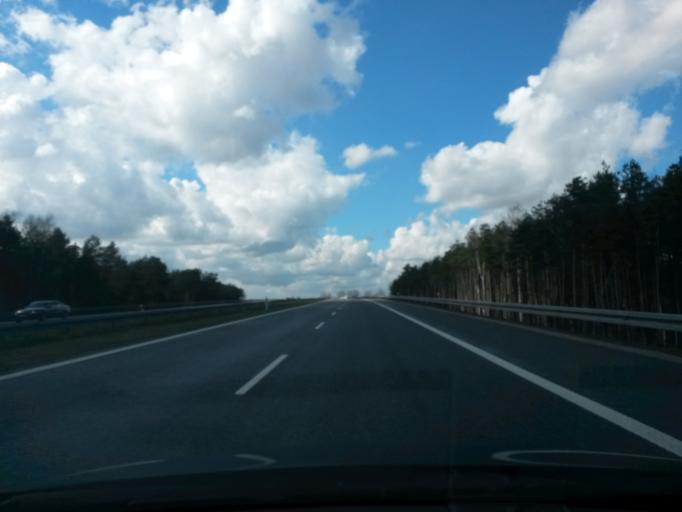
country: PL
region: Lodz Voivodeship
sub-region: Powiat leczycki
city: Swinice Warckie
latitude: 52.0252
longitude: 18.9192
